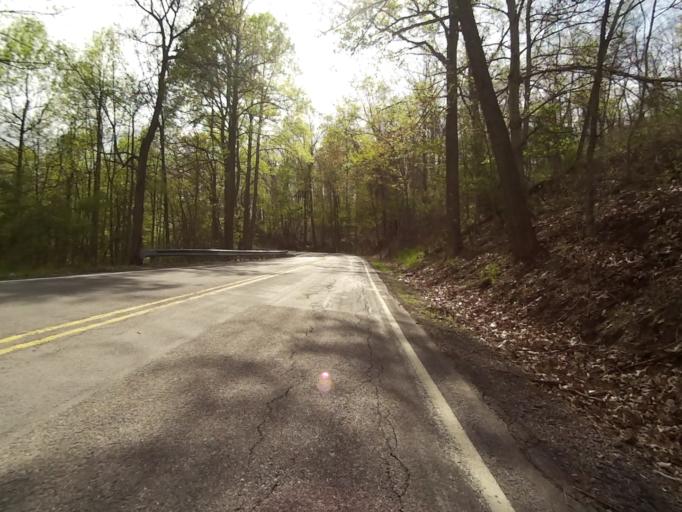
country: US
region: Pennsylvania
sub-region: Centre County
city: Stormstown
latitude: 40.8851
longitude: -77.9884
